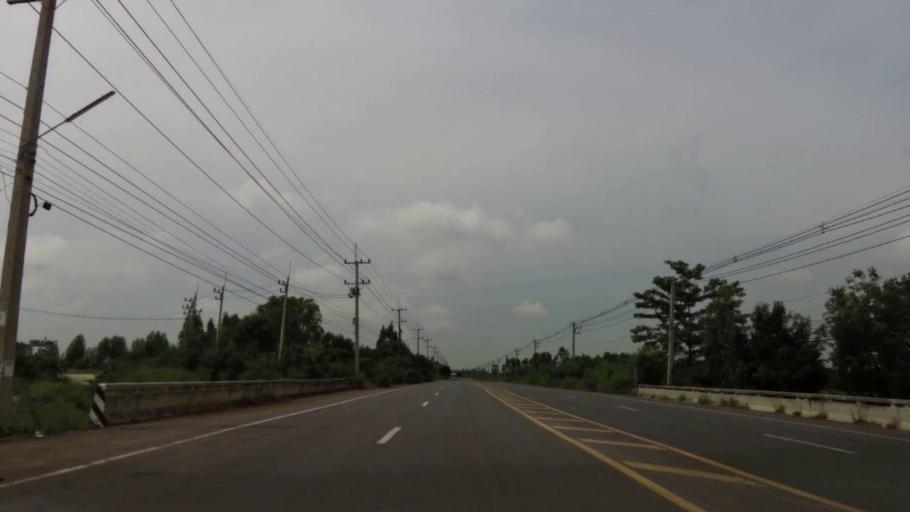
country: TH
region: Lop Buri
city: Khok Samrong
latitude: 15.0652
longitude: 100.6342
